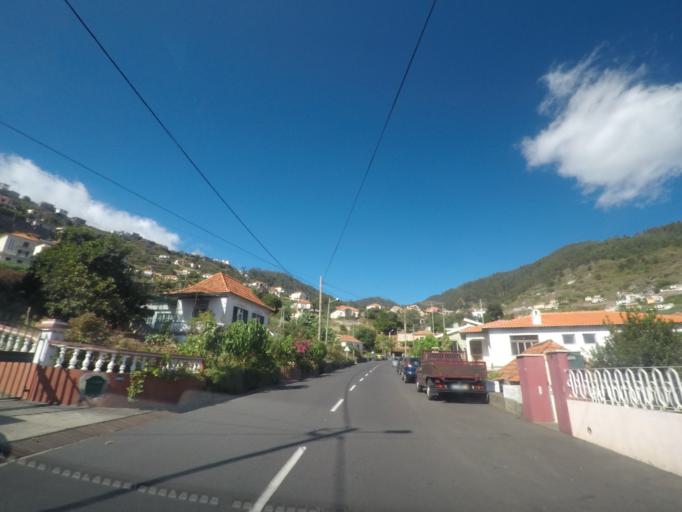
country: PT
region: Madeira
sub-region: Ribeira Brava
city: Campanario
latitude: 32.6742
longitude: -17.0275
